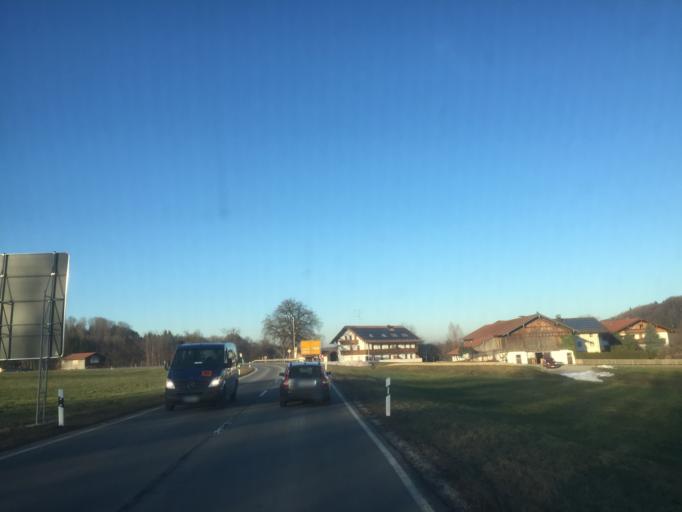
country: DE
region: Bavaria
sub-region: Upper Bavaria
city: Vachendorf
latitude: 47.8506
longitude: 12.6324
